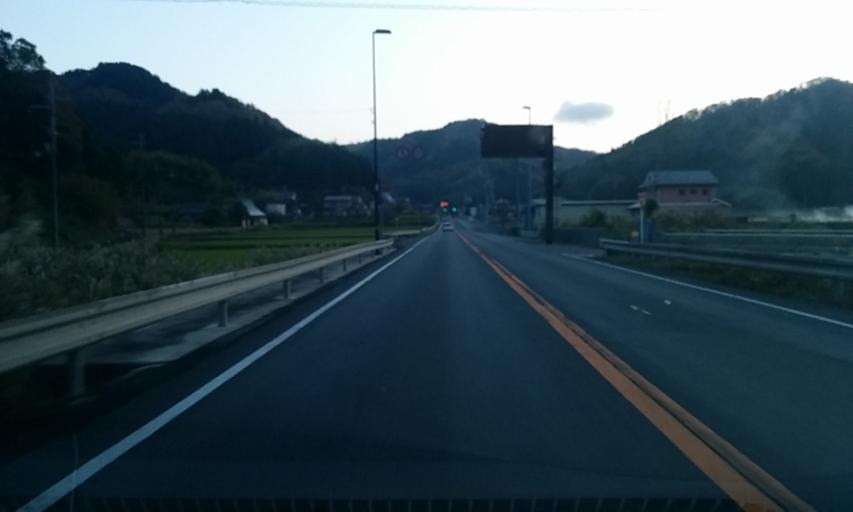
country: JP
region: Kyoto
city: Kameoka
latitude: 35.1442
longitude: 135.4270
